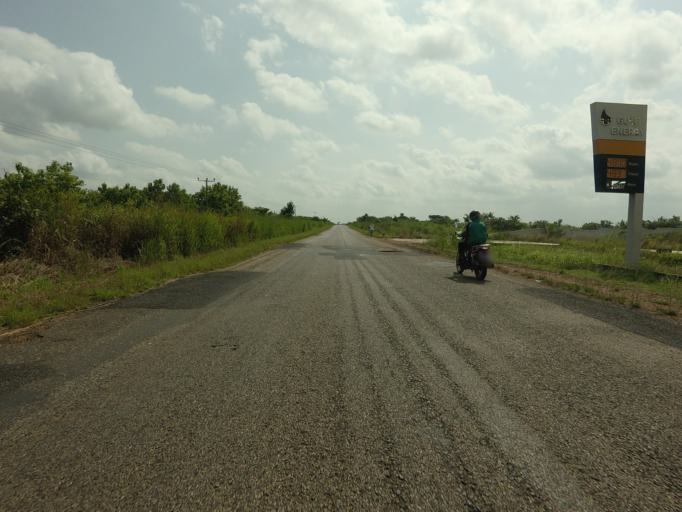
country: TG
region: Maritime
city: Tsevie
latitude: 6.3922
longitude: 0.8274
